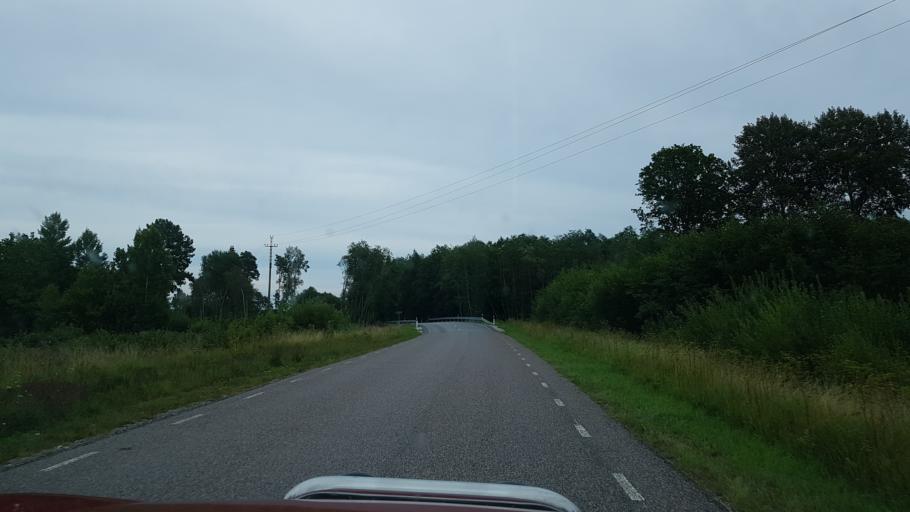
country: EE
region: Laeaene
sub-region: Lihula vald
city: Lihula
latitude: 58.8787
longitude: 23.8192
